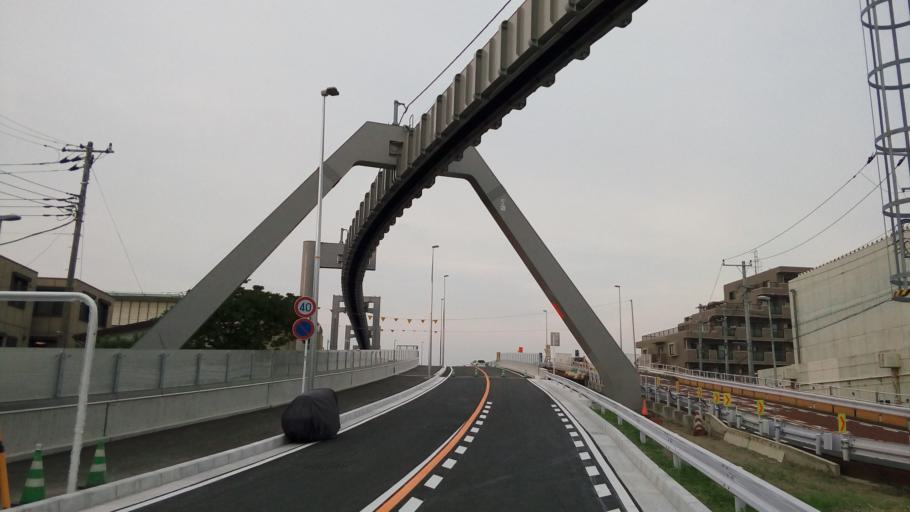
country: JP
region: Kanagawa
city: Kamakura
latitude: 35.3464
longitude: 139.5303
